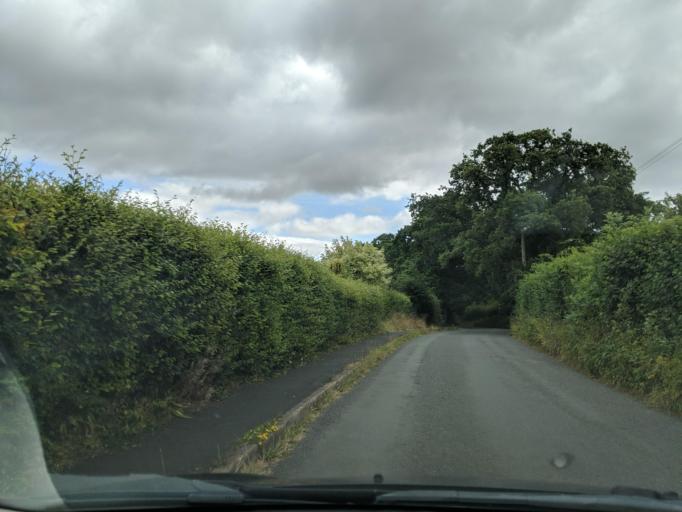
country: GB
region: England
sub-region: Devon
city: Totnes
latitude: 50.4429
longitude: -3.7129
